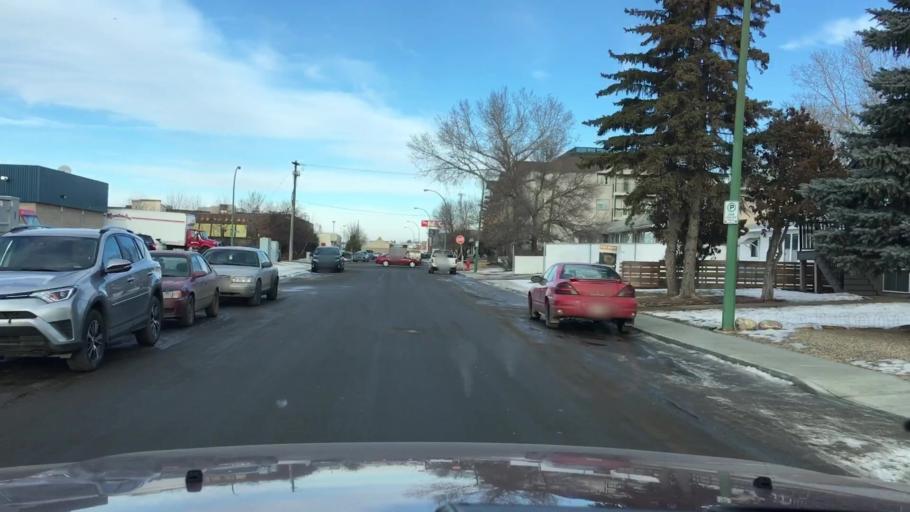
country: CA
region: Saskatchewan
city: Regina
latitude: 50.4781
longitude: -104.6166
